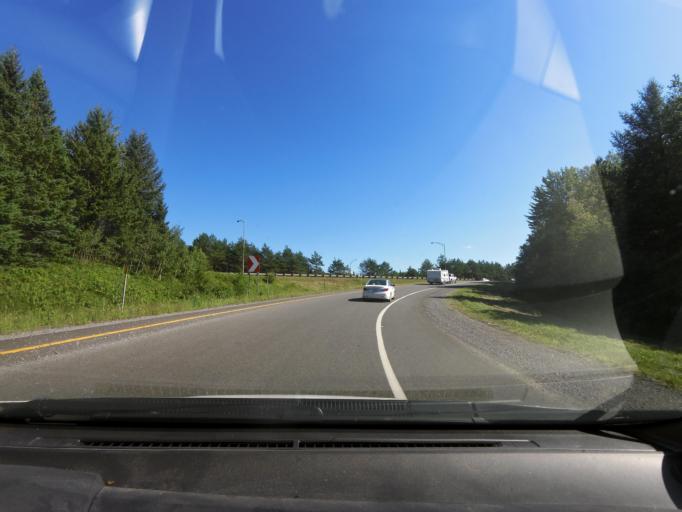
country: CA
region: Quebec
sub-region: Mauricie
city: Becancour
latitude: 46.5151
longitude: -72.2941
